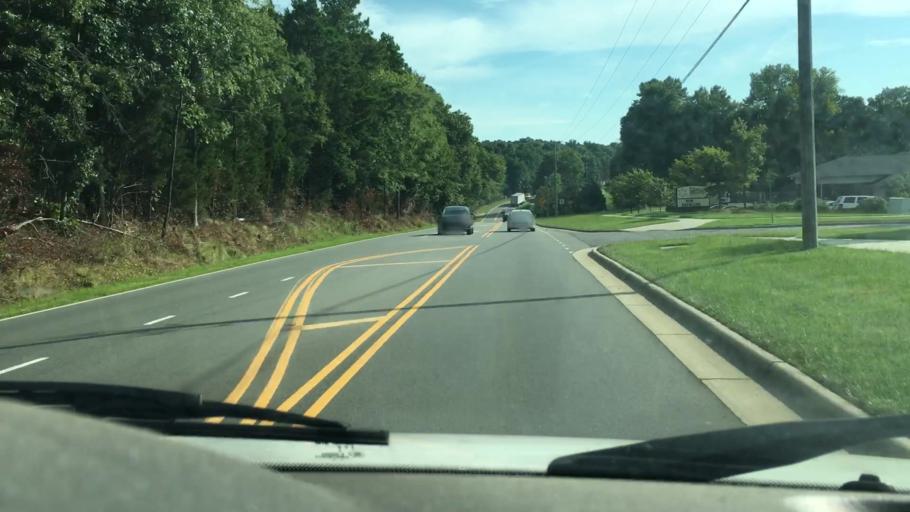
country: US
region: North Carolina
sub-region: Mecklenburg County
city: Huntersville
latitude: 35.3785
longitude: -80.7970
